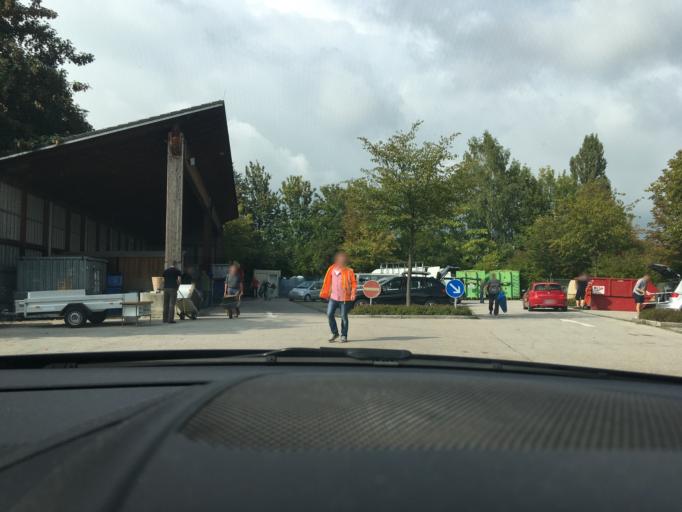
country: DE
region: Bavaria
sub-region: Upper Bavaria
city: Ismaning
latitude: 48.2303
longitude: 11.6804
